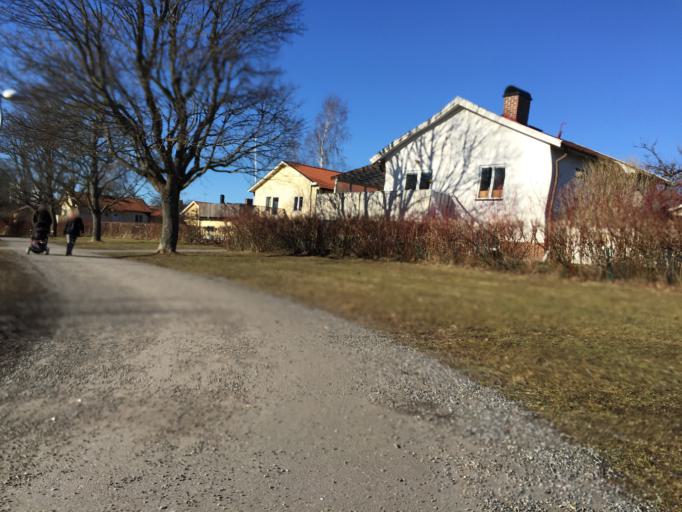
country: SE
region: Stockholm
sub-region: Stockholms Kommun
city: Bromma
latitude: 59.3617
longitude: 17.8888
